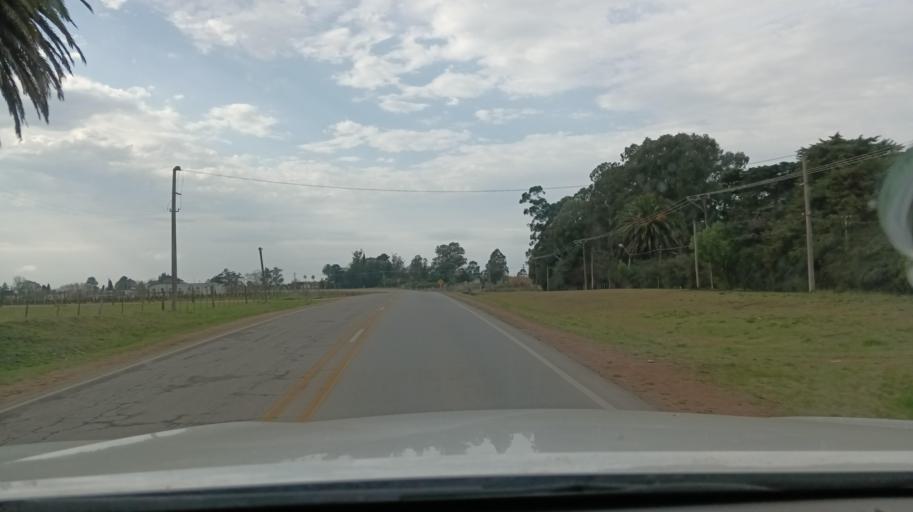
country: UY
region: Canelones
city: Toledo
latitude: -34.7087
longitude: -56.1078
